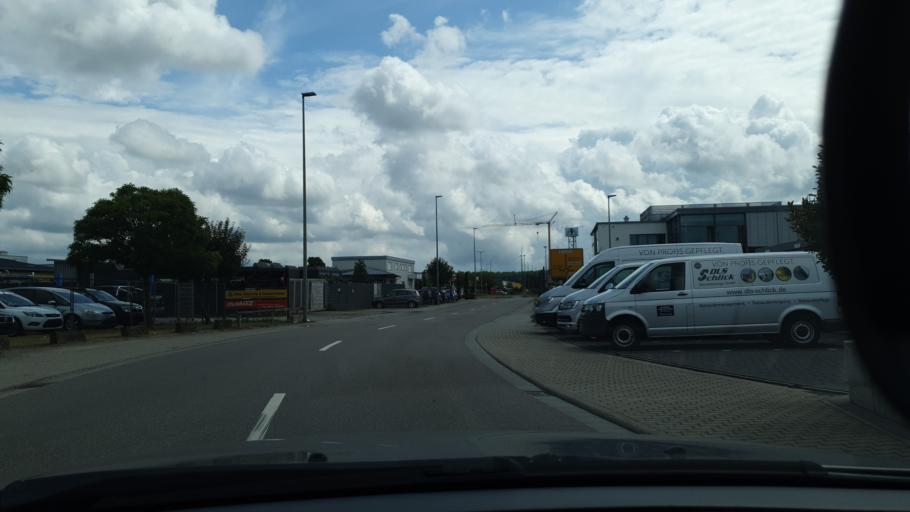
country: DE
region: Rheinland-Pfalz
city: Offenbach an der Queich
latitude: 49.2009
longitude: 8.2056
